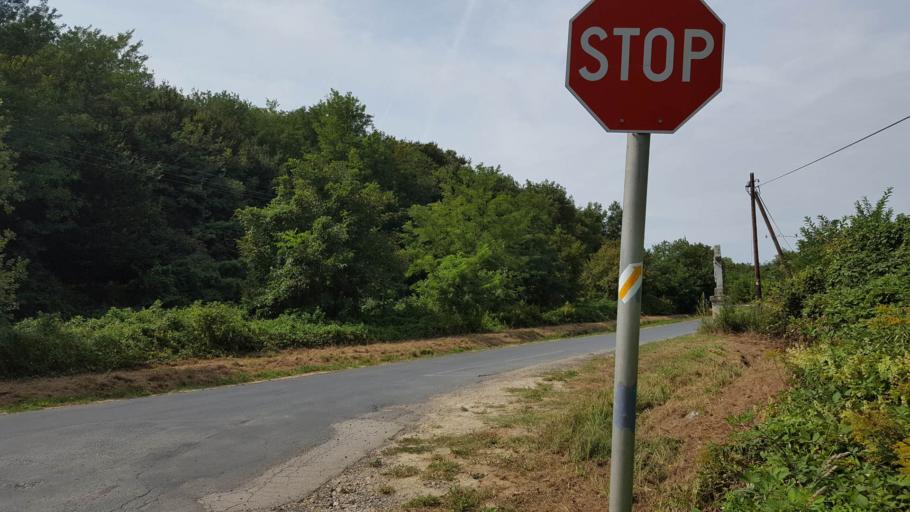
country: HU
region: Somogy
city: Somogyvar
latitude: 46.5817
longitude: 17.6744
